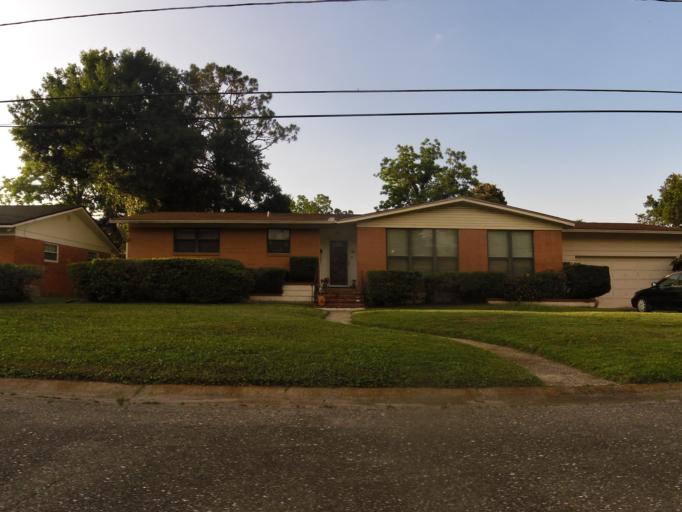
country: US
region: Florida
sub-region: Clay County
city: Orange Park
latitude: 30.2248
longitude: -81.6133
